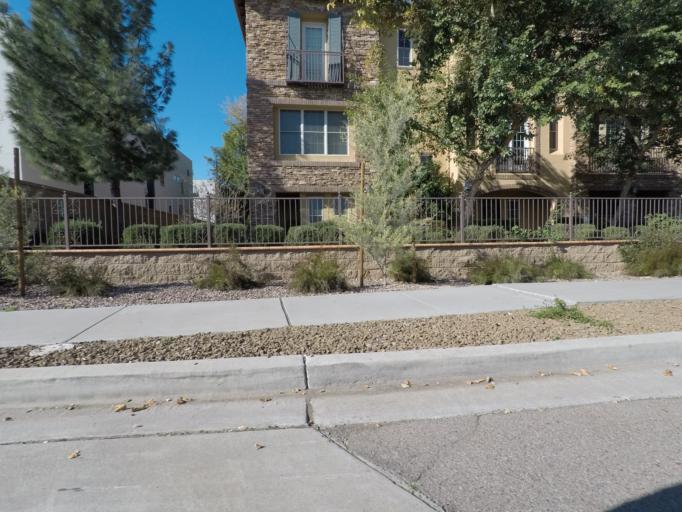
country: US
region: Arizona
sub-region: Maricopa County
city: Phoenix
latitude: 33.4997
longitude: -112.0281
